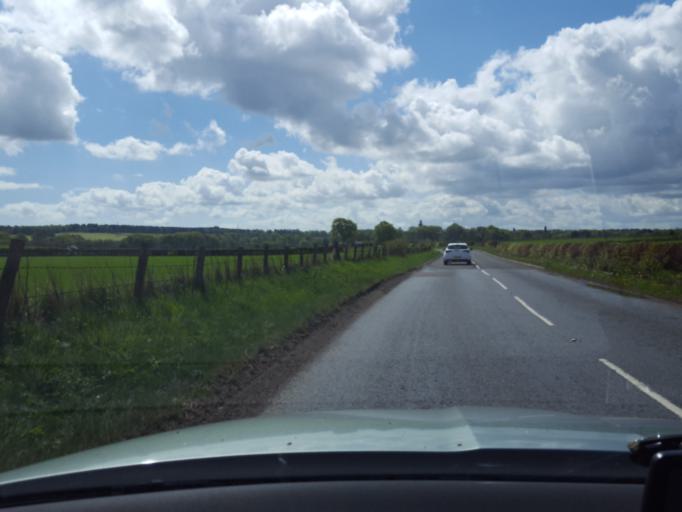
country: GB
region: Scotland
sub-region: Angus
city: Brechin
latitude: 56.7774
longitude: -2.6442
